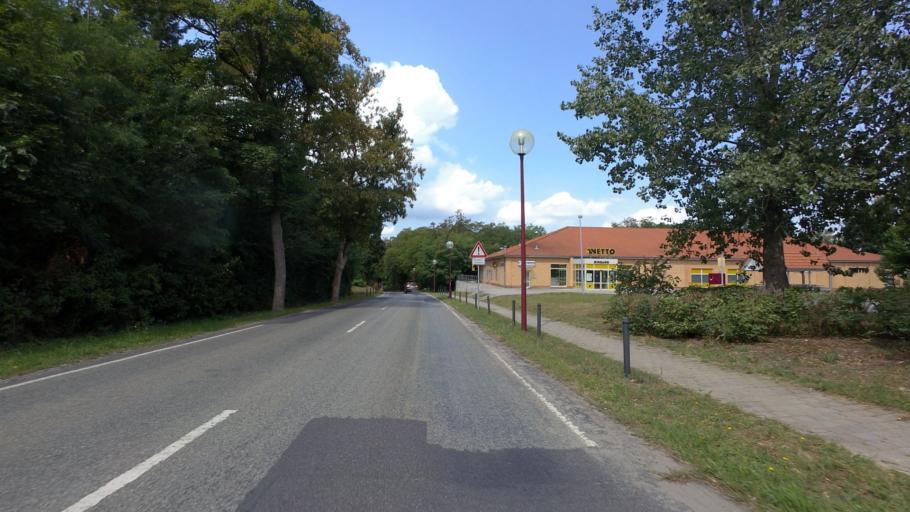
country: DE
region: Brandenburg
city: Teupitz
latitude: 52.1320
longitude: 13.6203
